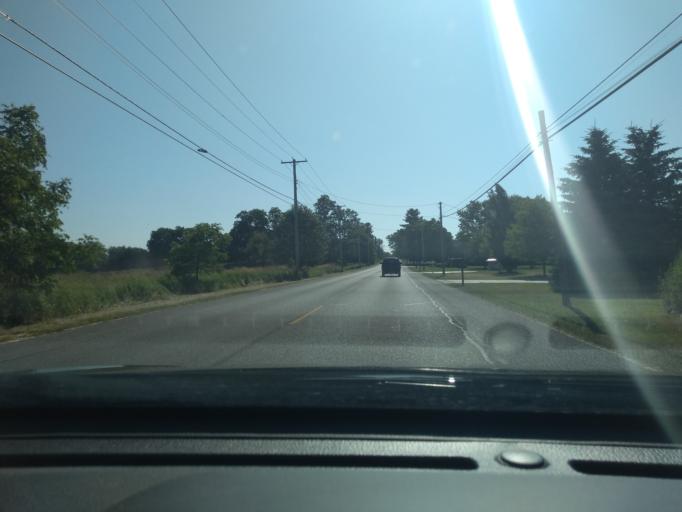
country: US
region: New York
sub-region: Erie County
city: Orchard Park
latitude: 42.7891
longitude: -78.7371
